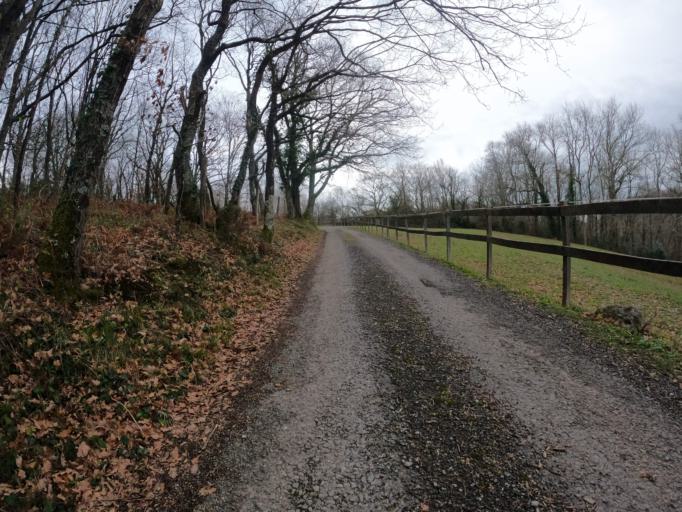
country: FR
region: Aquitaine
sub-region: Departement des Pyrenees-Atlantiques
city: Mazeres-Lezons
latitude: 43.2694
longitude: -0.3555
